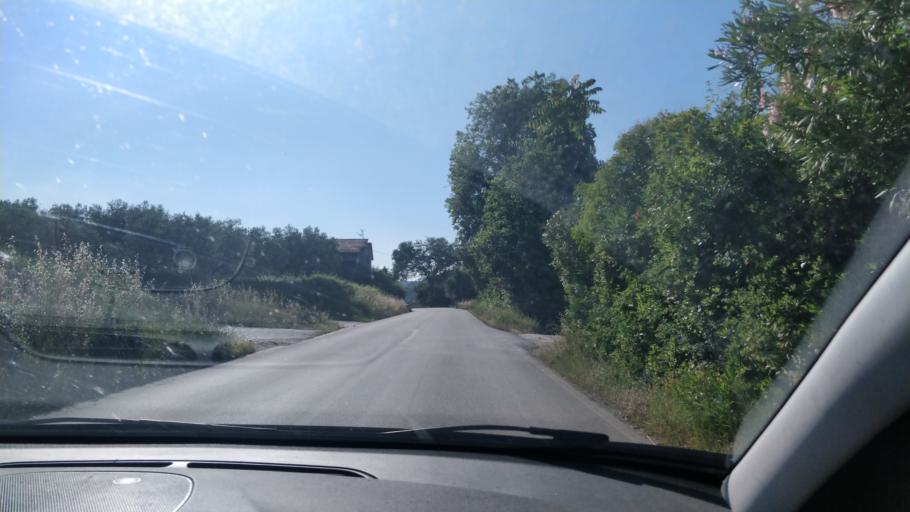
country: IT
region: The Marches
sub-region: Provincia di Ascoli Piceno
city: Cupra Marittima
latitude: 43.0352
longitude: 13.8442
